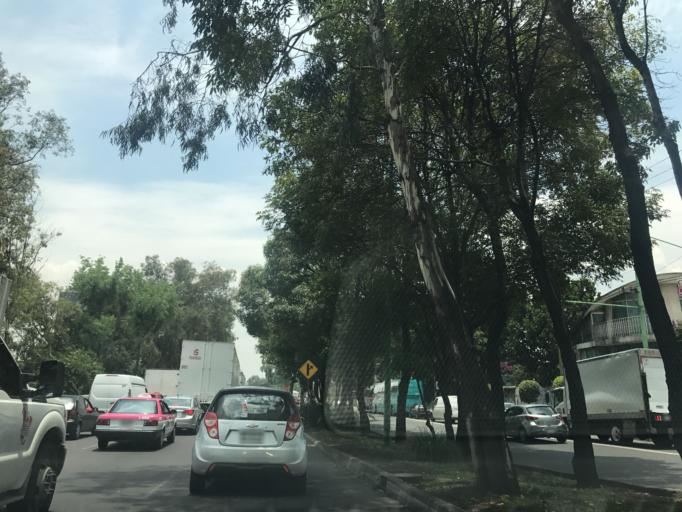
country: MX
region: Mexico
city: Colonia Lindavista
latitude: 19.4872
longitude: -99.1435
